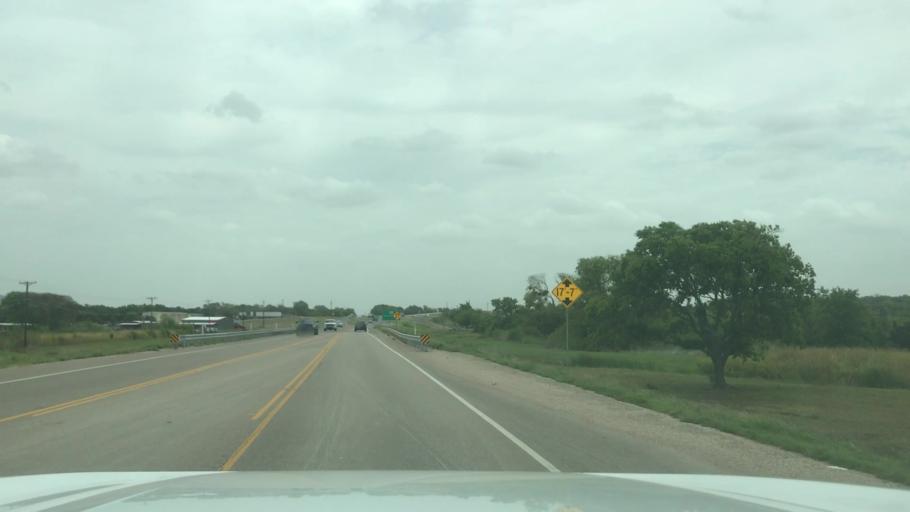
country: US
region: Texas
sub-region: McLennan County
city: Woodway
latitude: 31.5777
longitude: -97.2962
